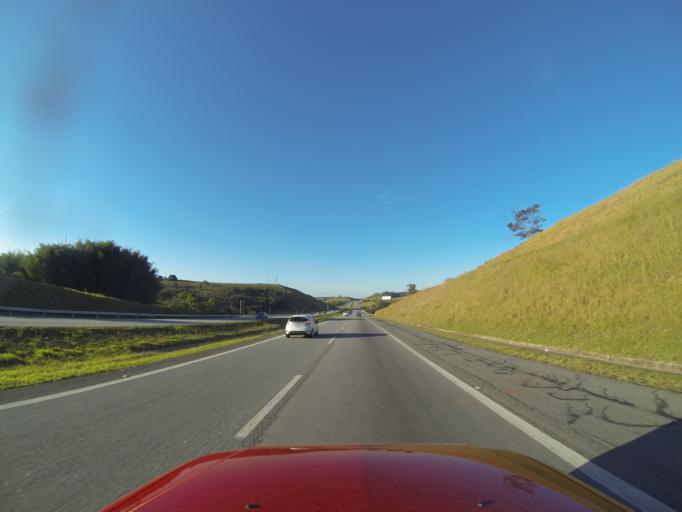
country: BR
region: Sao Paulo
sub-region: Jacarei
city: Jacarei
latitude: -23.3124
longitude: -45.8987
